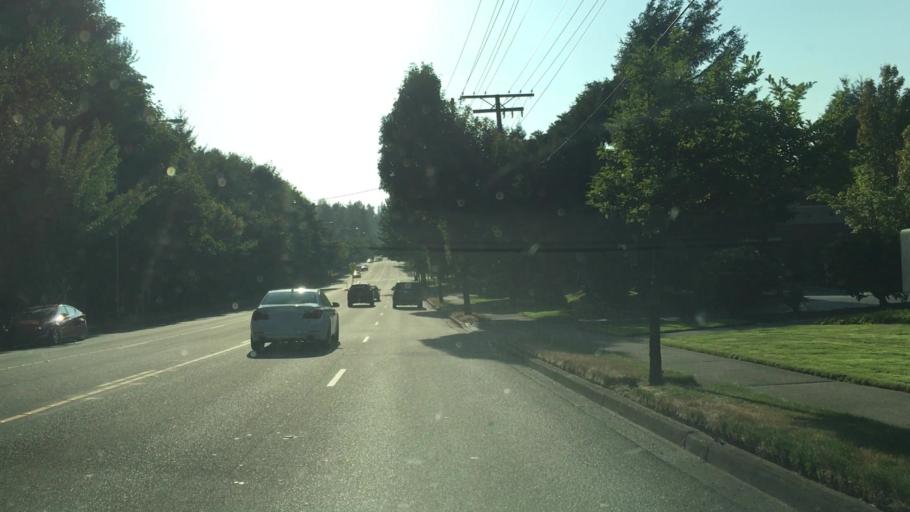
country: US
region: Washington
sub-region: King County
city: Federal Way
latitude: 47.2899
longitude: -122.3242
